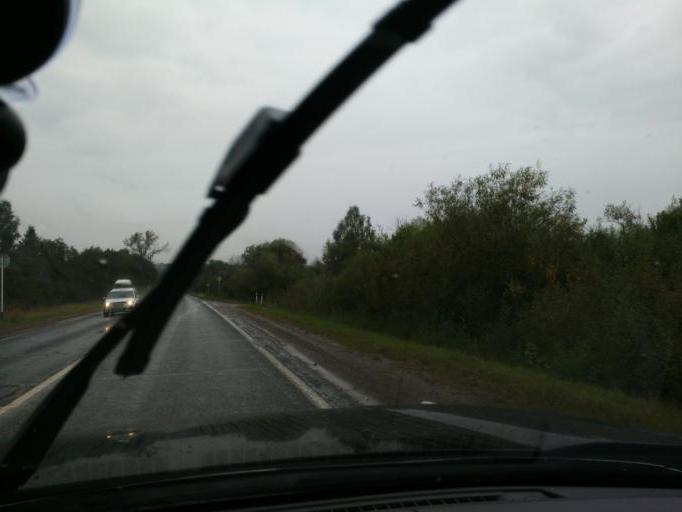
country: RU
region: Perm
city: Yugo-Kamskiy
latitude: 57.5344
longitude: 55.6898
